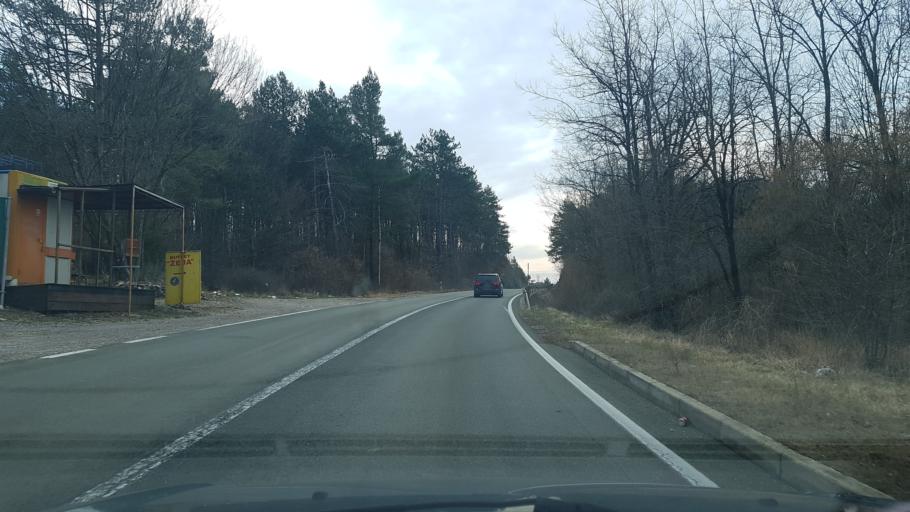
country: SI
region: Ilirska Bistrica
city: Ilirska Bistrica
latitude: 45.4787
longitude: 14.2636
